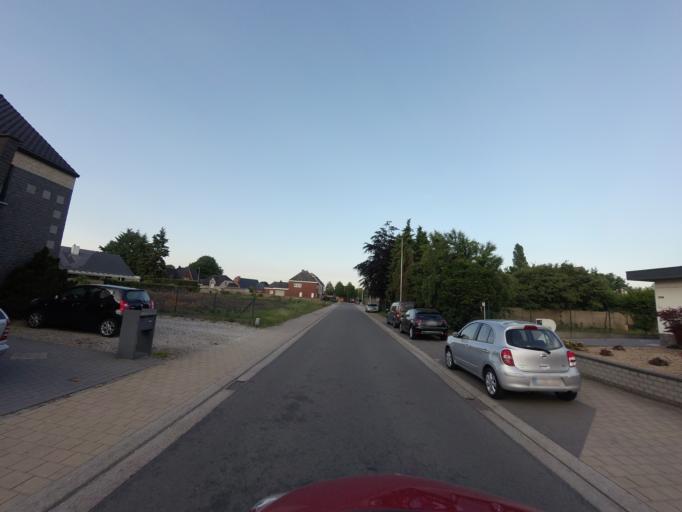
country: BE
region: Flanders
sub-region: Provincie Limburg
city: Lommel
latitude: 51.2322
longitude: 5.3294
